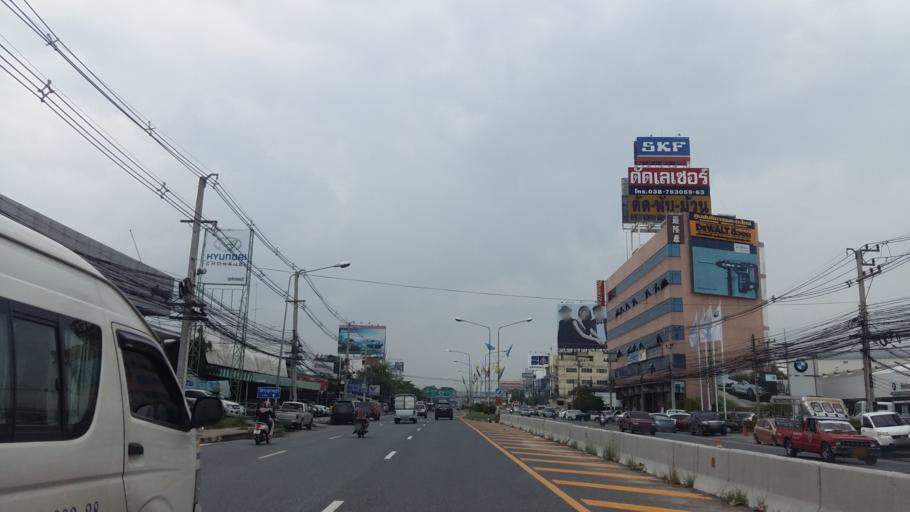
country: TH
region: Chon Buri
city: Chon Buri
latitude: 13.3386
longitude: 100.9728
